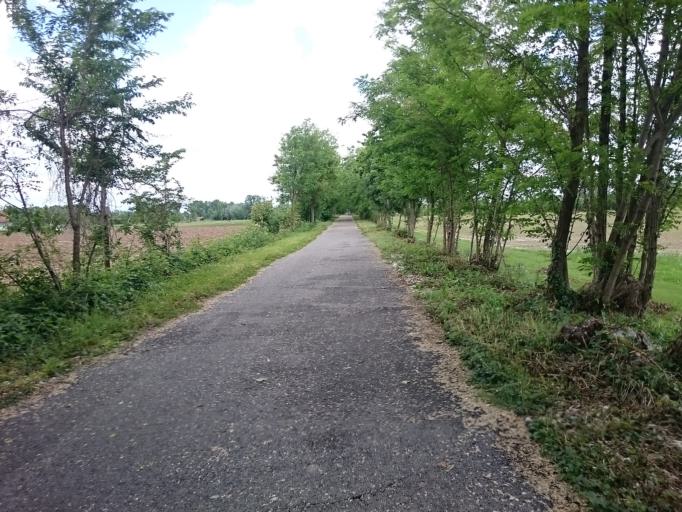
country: IT
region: Veneto
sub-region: Provincia di Padova
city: Campodoro
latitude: 45.5164
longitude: 11.7571
